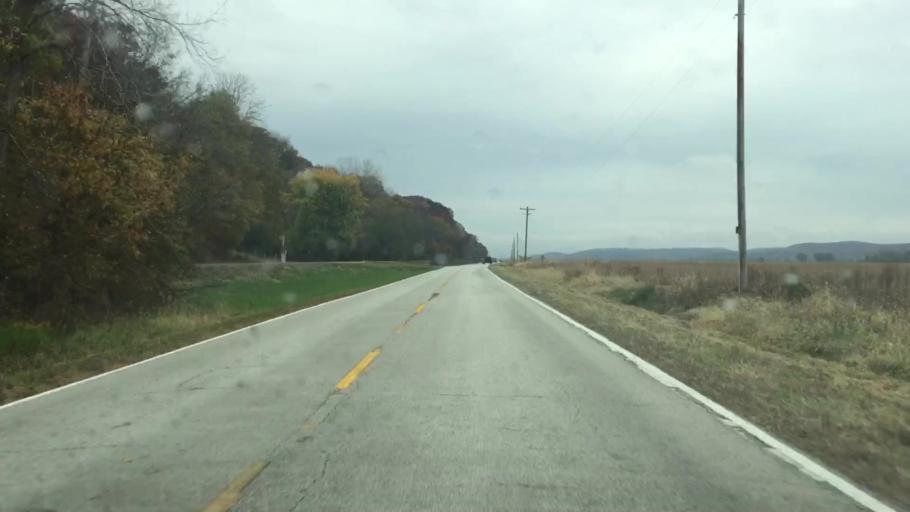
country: US
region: Missouri
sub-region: Gasconade County
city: Hermann
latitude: 38.7024
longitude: -91.5832
